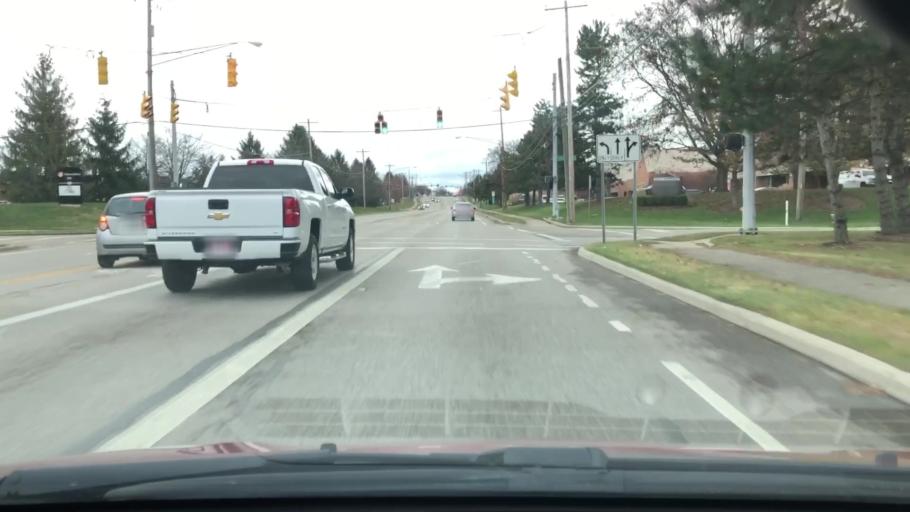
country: US
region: Ohio
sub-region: Franklin County
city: Westerville
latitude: 40.1102
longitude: -82.9364
